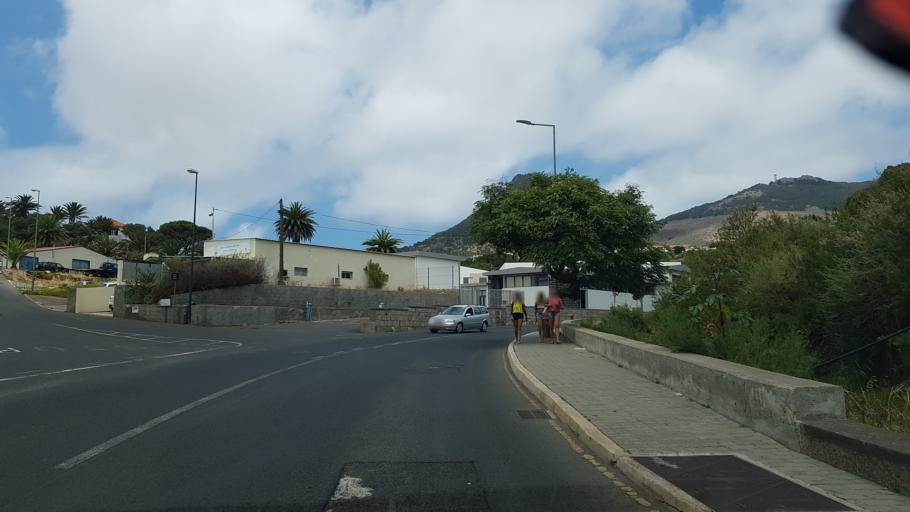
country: PT
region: Madeira
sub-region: Porto Santo
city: Vila de Porto Santo
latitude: 33.0631
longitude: -16.3353
